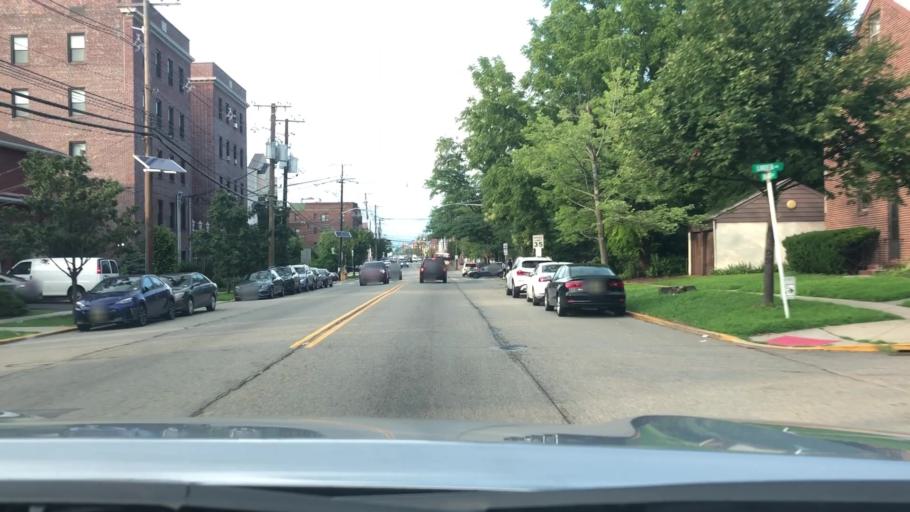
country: US
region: New Jersey
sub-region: Bergen County
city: Ridgefield
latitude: 40.8409
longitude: -74.0030
